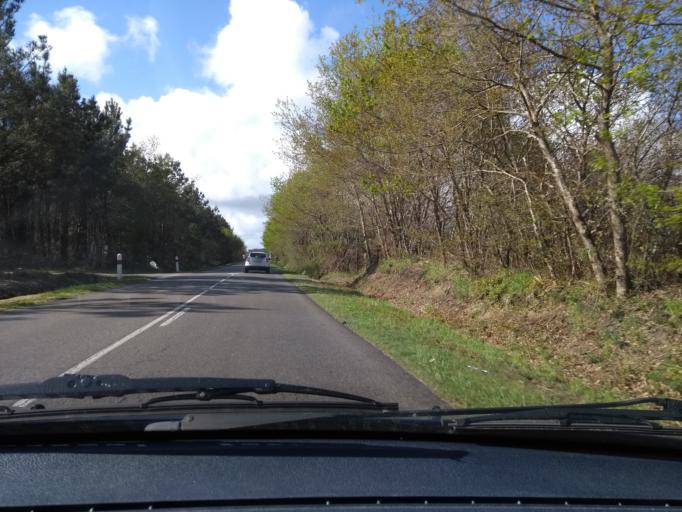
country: FR
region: Aquitaine
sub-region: Departement des Landes
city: Parentis-en-Born
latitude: 44.3378
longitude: -1.0838
